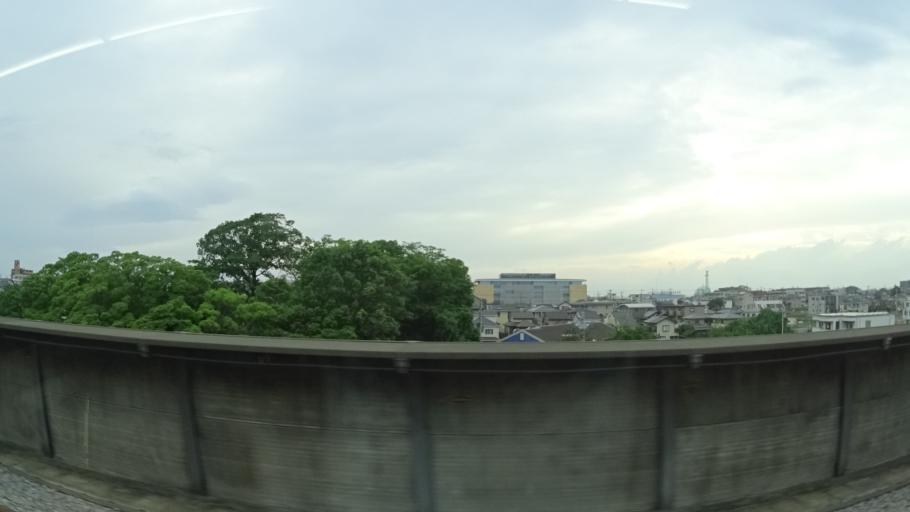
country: JP
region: Saitama
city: Yono
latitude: 35.8659
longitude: 139.6317
